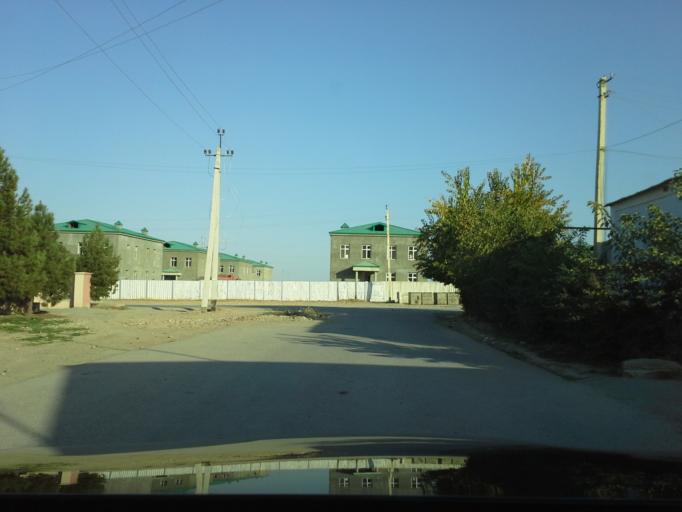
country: TM
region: Ahal
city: Abadan
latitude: 38.0456
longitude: 58.1680
